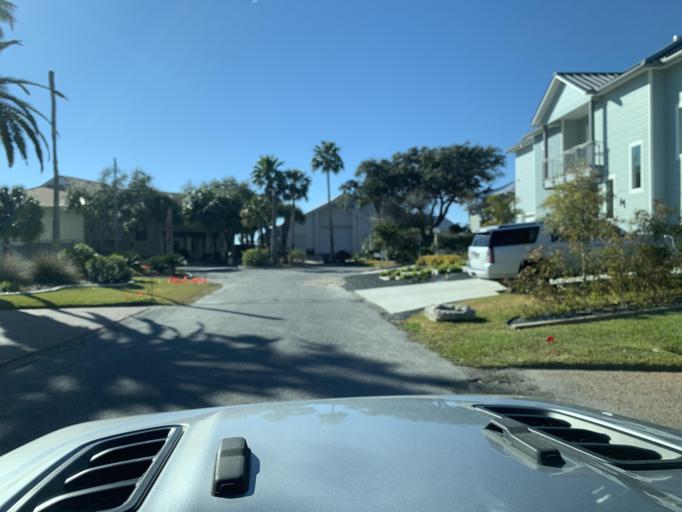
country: US
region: Texas
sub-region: Aransas County
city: Fulton
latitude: 28.0378
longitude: -97.0311
